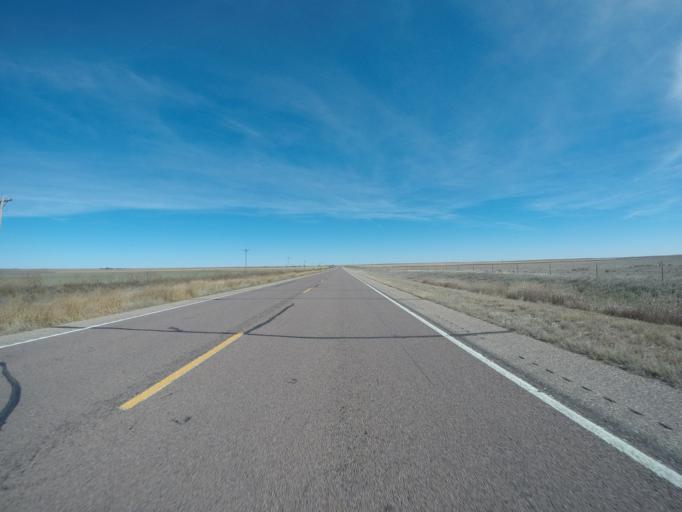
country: US
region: Colorado
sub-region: Kit Carson County
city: Burlington
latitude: 39.6581
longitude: -102.5325
